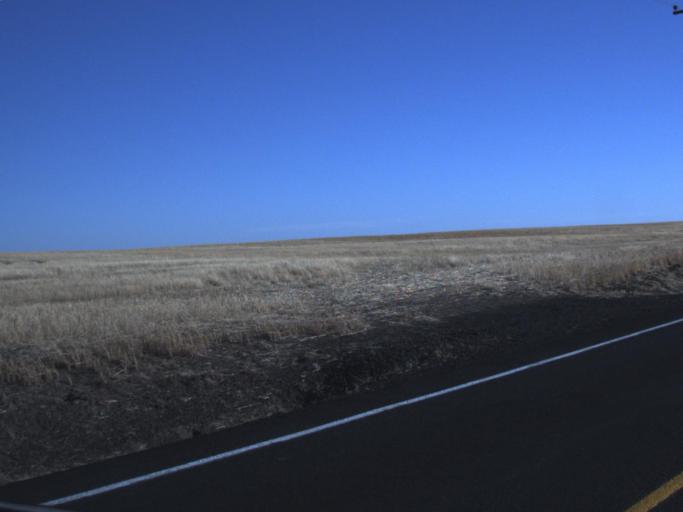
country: US
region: Washington
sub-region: Adams County
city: Ritzville
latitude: 46.9455
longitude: -118.3434
